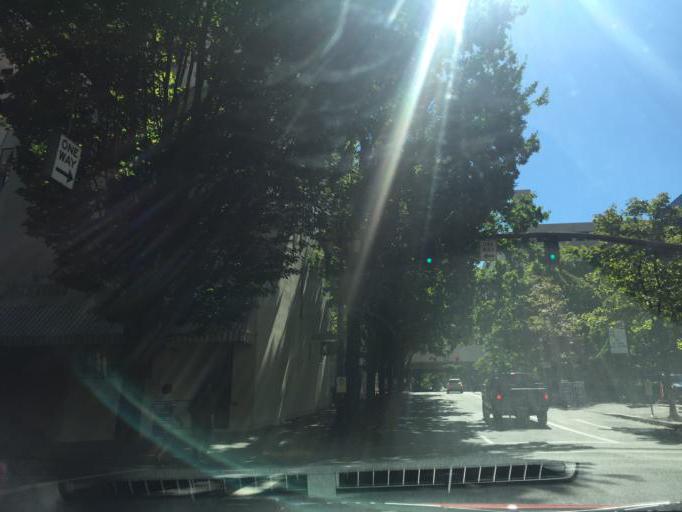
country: US
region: Oregon
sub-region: Multnomah County
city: Portland
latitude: 45.5131
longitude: -122.6761
